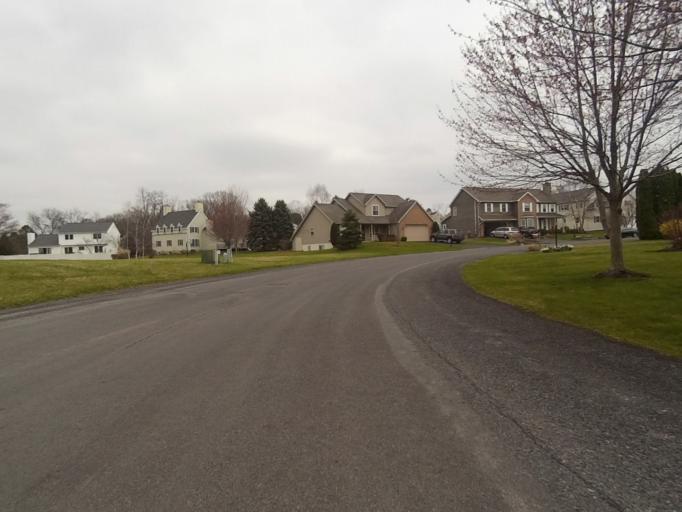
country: US
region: Pennsylvania
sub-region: Centre County
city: Boalsburg
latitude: 40.7853
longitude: -77.7798
